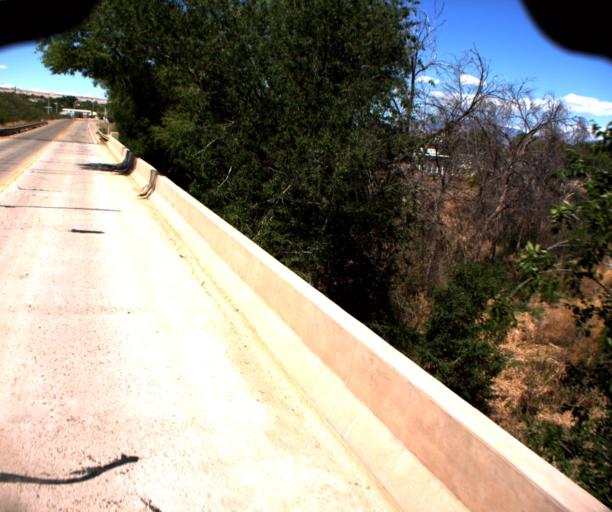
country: US
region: Arizona
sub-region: Cochise County
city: Benson
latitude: 31.9650
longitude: -110.2790
